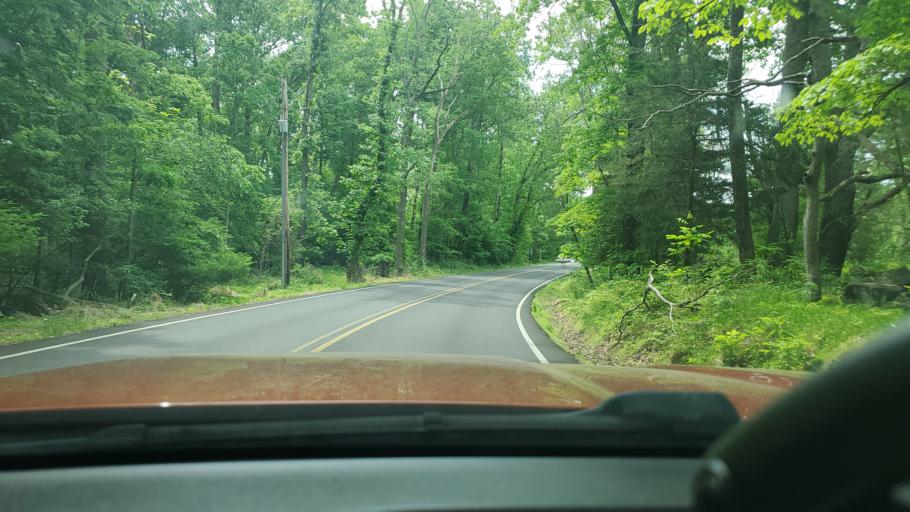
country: US
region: Pennsylvania
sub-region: Montgomery County
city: Woxall
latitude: 40.3284
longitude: -75.4837
